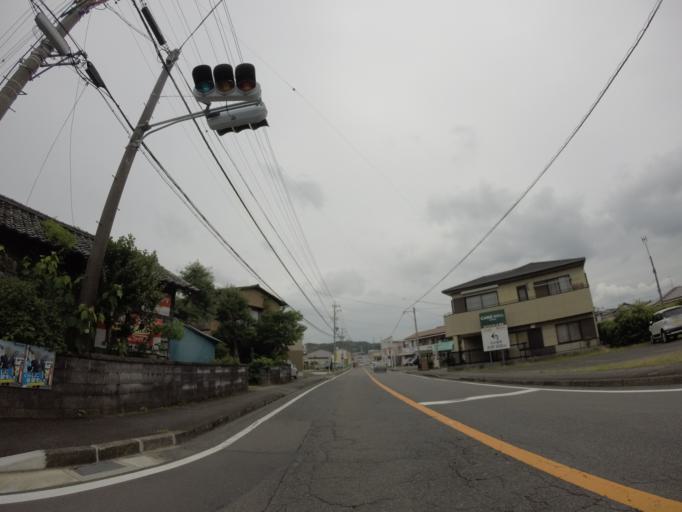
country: JP
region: Shizuoka
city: Fujieda
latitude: 34.8503
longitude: 138.2430
